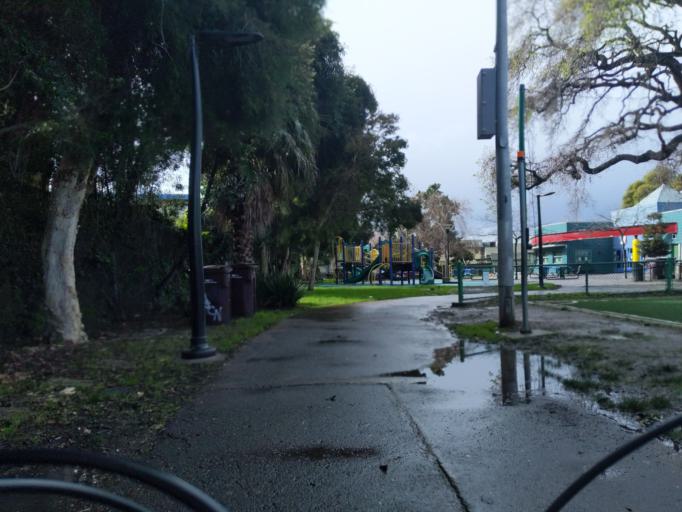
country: US
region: California
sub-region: Alameda County
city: Alameda
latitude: 37.7806
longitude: -122.2253
